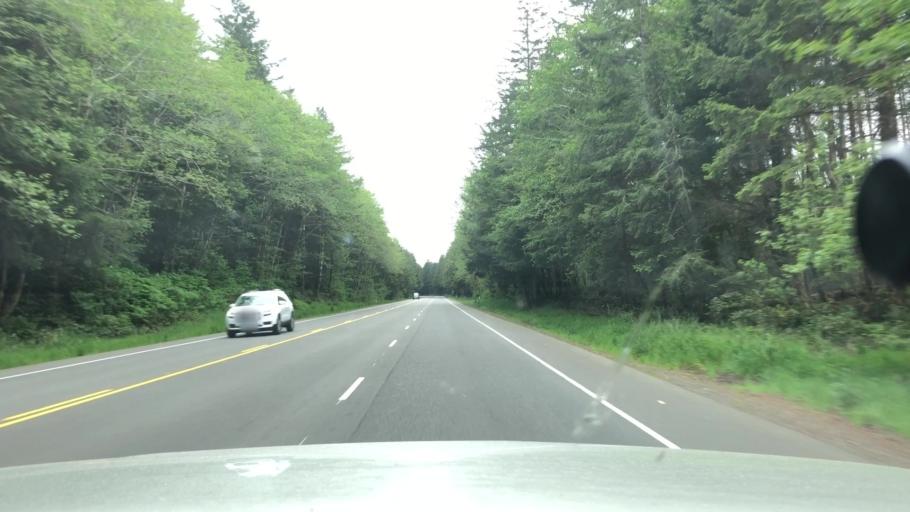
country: US
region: Oregon
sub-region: Coos County
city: Coquille
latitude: 43.2224
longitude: -124.3018
